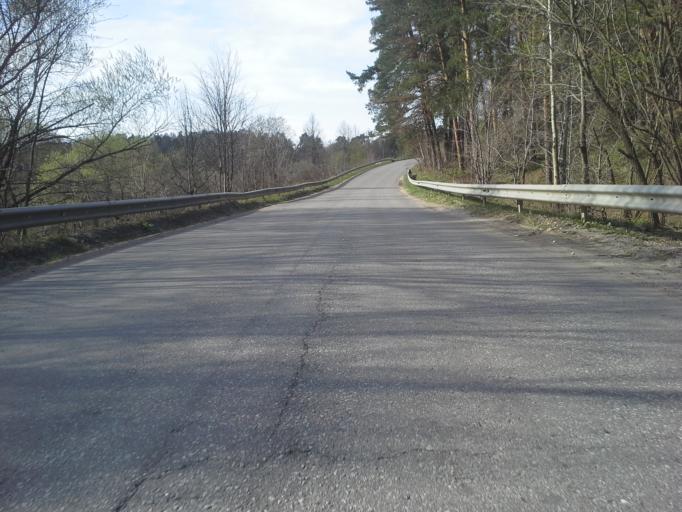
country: RU
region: Moskovskaya
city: Vatutinki
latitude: 55.4481
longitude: 37.3993
